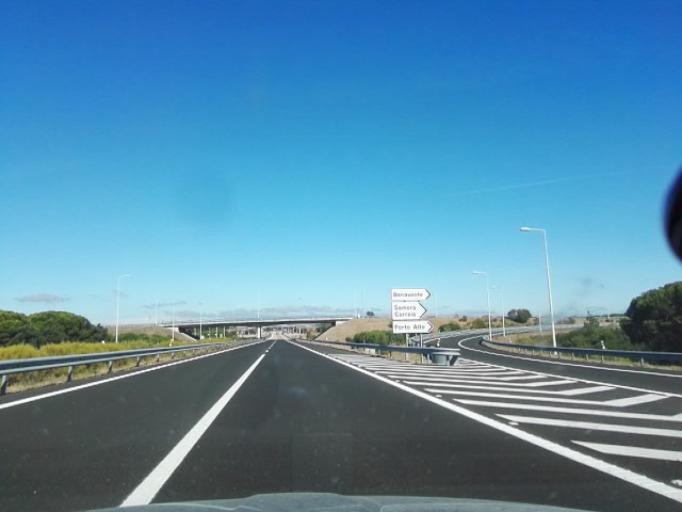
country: PT
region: Santarem
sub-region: Benavente
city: Benavente
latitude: 38.9537
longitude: -8.8265
